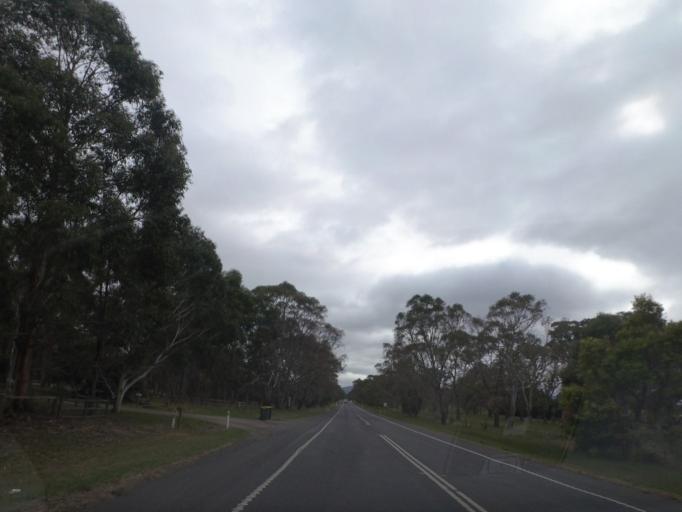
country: AU
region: Victoria
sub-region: Whittlesea
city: Mernda
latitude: -37.5634
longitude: 145.1092
